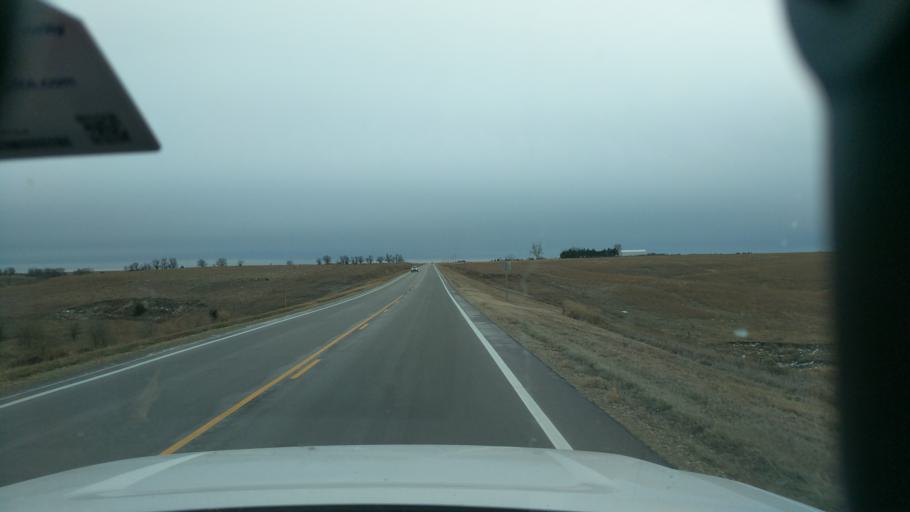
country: US
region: Kansas
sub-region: Dickinson County
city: Herington
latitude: 38.7814
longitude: -96.9273
